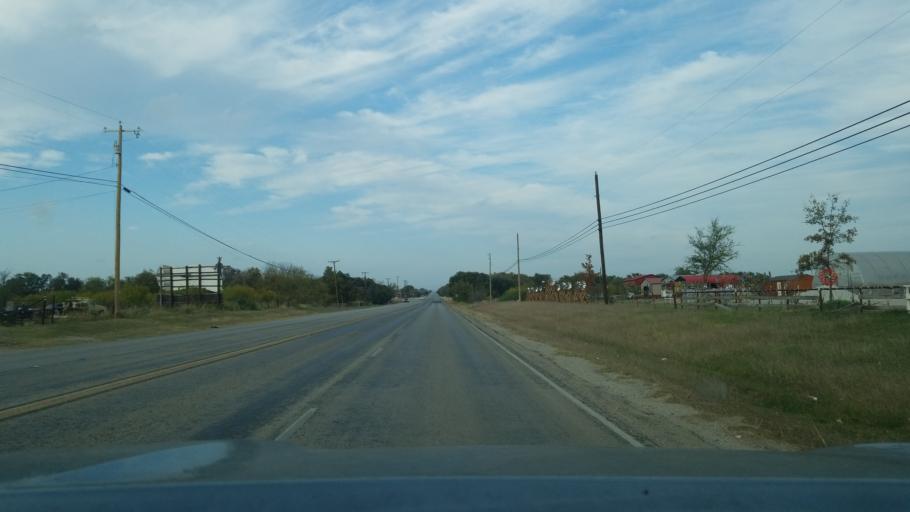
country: US
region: Texas
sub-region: Brown County
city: Early
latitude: 31.7531
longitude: -98.9613
